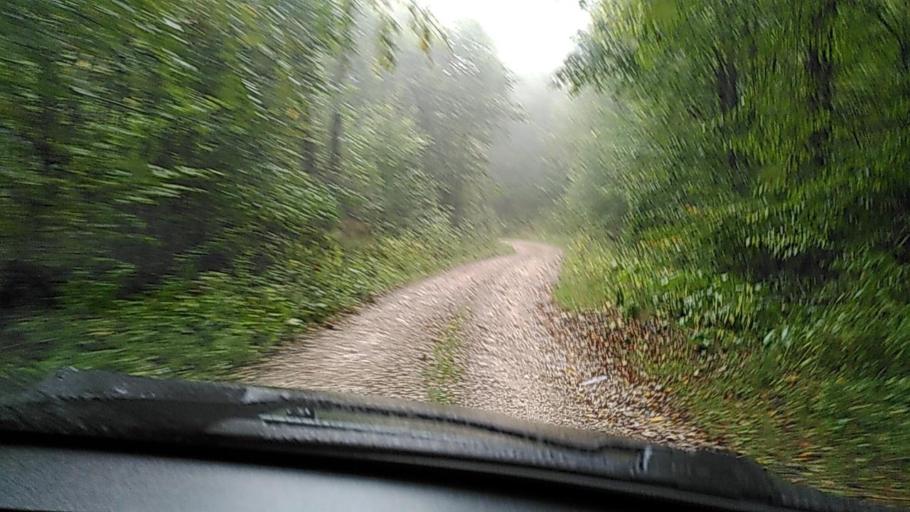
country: RU
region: Kabardino-Balkariya
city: Belaya Rechka
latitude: 43.3730
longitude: 43.4275
